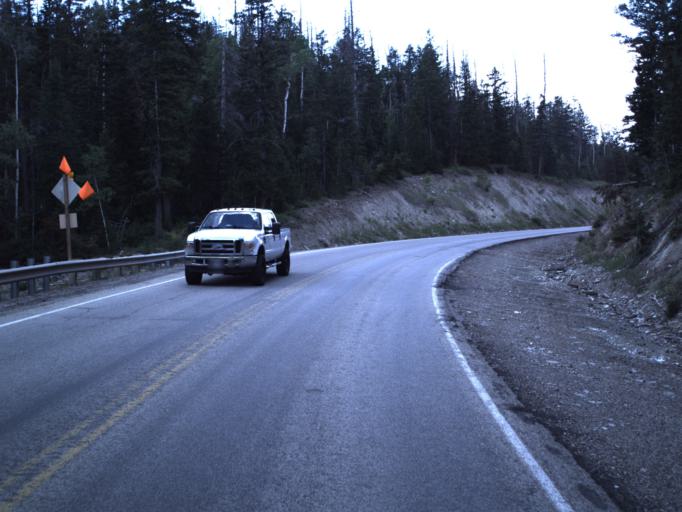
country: US
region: Utah
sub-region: Carbon County
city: Helper
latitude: 39.8953
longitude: -110.7484
